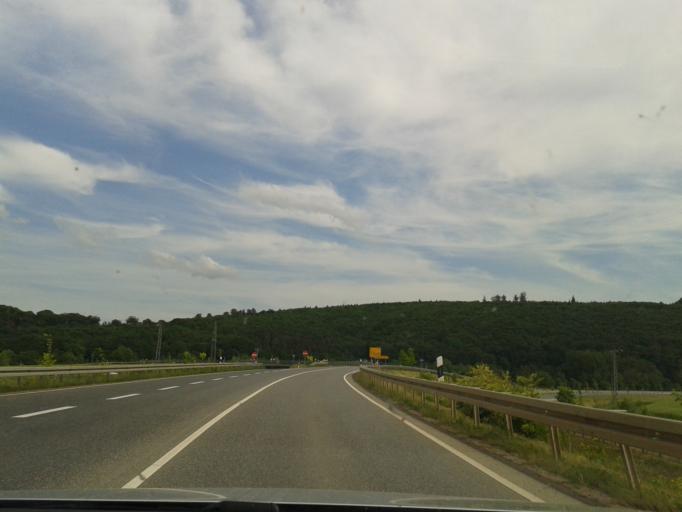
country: DE
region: Hesse
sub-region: Regierungsbezirk Giessen
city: Marburg an der Lahn
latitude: 50.7541
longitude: 8.7385
